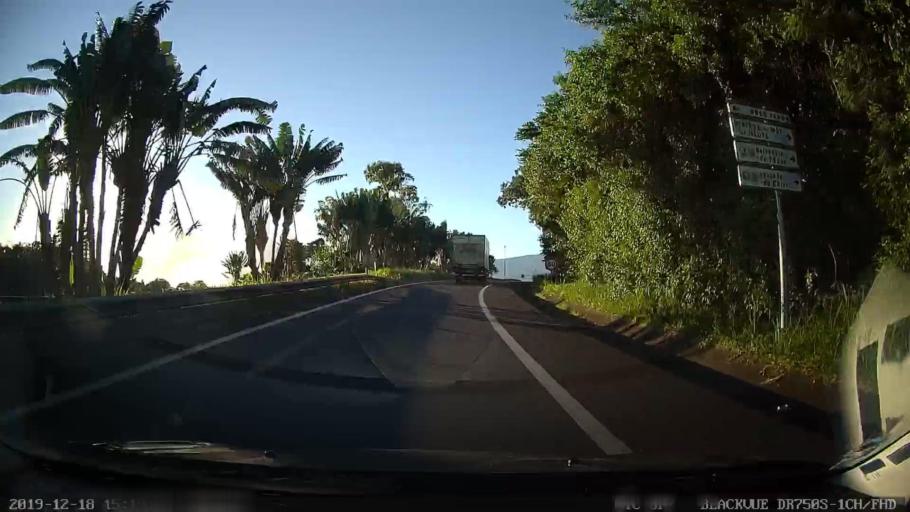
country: RE
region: Reunion
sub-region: Reunion
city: Bras-Panon
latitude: -20.9889
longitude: 55.6609
